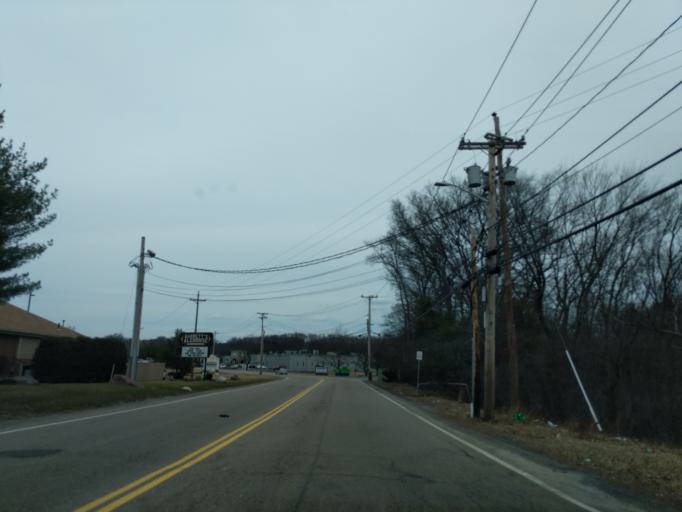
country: US
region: Massachusetts
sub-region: Bristol County
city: Attleboro
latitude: 41.9697
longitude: -71.2994
